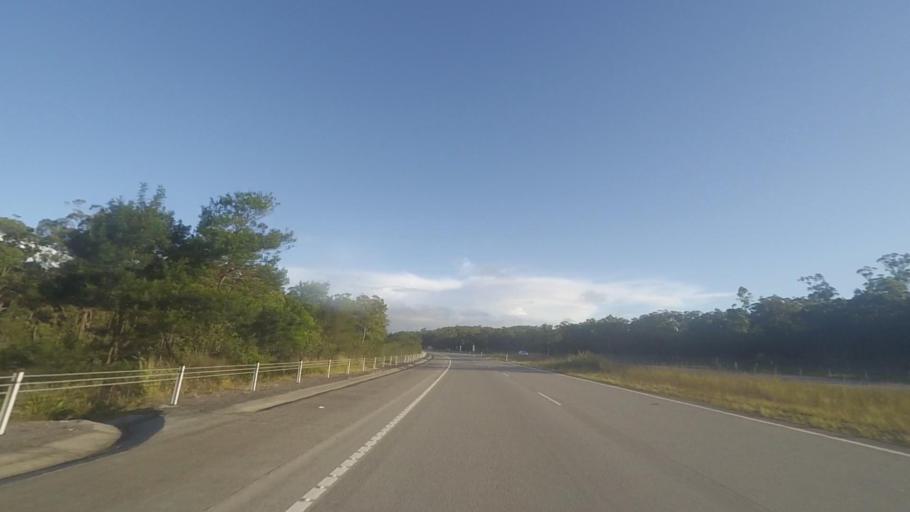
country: AU
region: New South Wales
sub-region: Great Lakes
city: Bulahdelah
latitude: -32.4847
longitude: 152.1936
